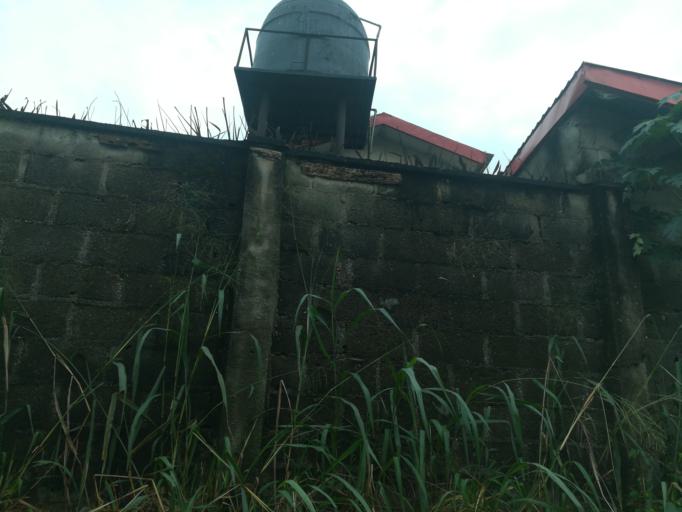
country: NG
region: Rivers
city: Port Harcourt
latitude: 4.8611
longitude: 7.0363
